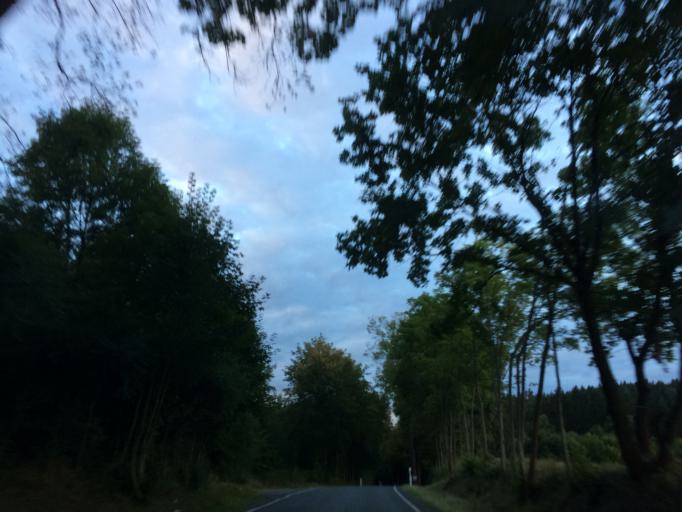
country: DE
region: Thuringia
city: Moxa
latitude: 50.6337
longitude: 11.6425
